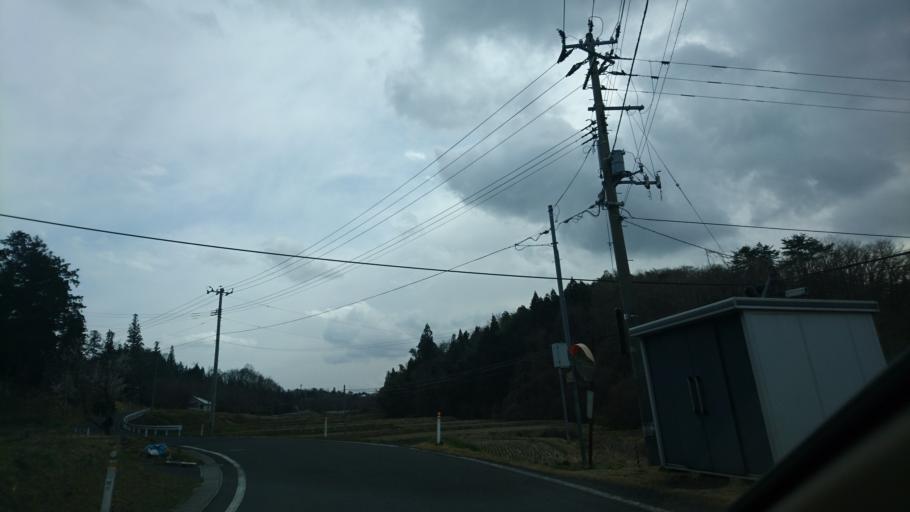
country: JP
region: Iwate
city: Ichinoseki
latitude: 38.8926
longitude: 141.1689
